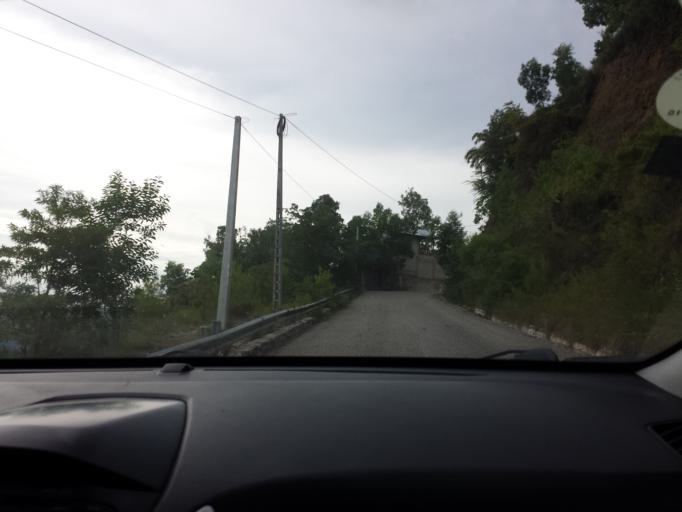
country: HT
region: Ouest
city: Leogane
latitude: 18.4036
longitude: -72.6399
